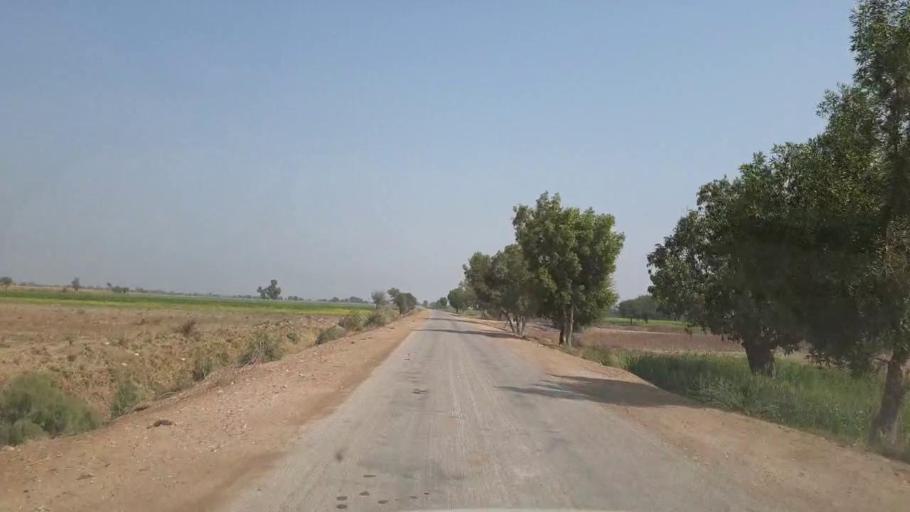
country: PK
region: Sindh
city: Mirpur Khas
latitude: 25.6455
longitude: 69.1567
